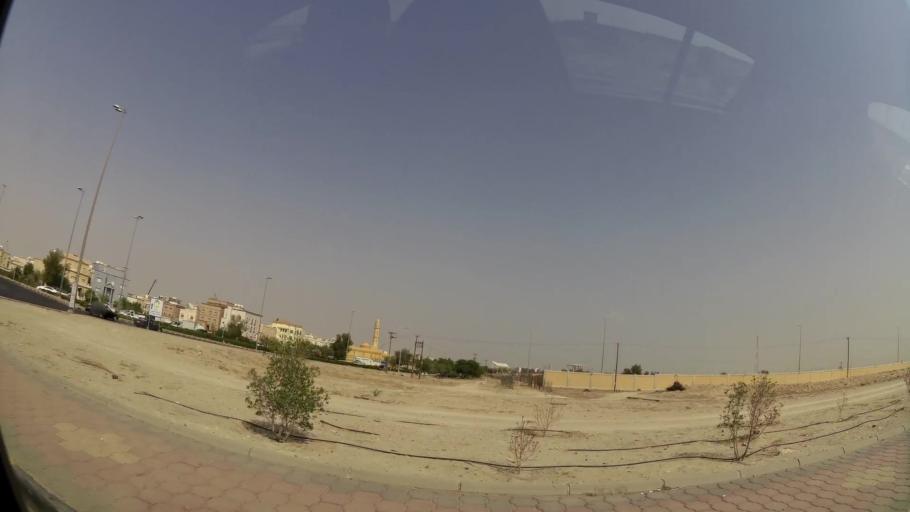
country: KW
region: Muhafazat al Jahra'
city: Al Jahra'
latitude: 29.3258
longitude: 47.7018
